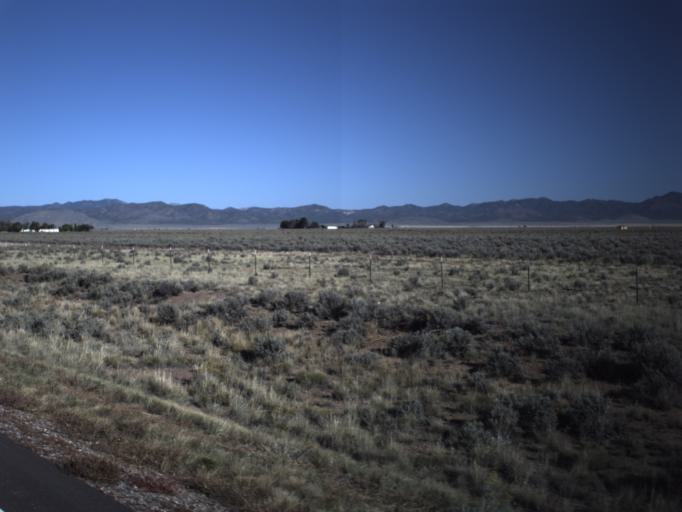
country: US
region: Utah
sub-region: Washington County
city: Enterprise
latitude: 37.7622
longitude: -113.8050
